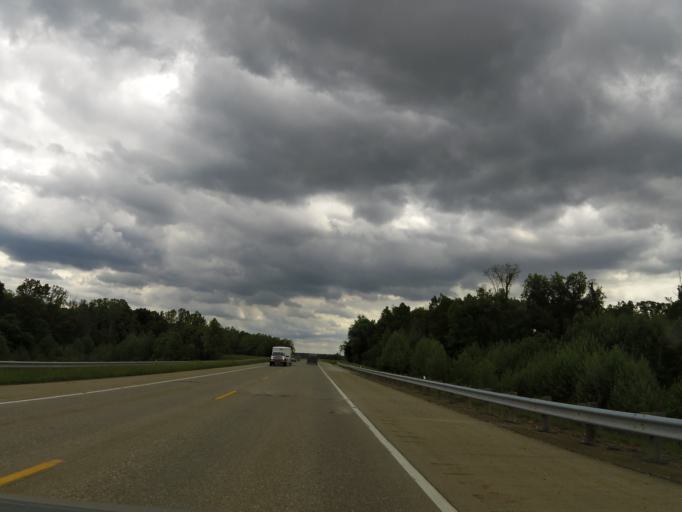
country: US
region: West Virginia
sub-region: Jackson County
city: Ravenswood
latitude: 38.9460
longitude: -81.7955
